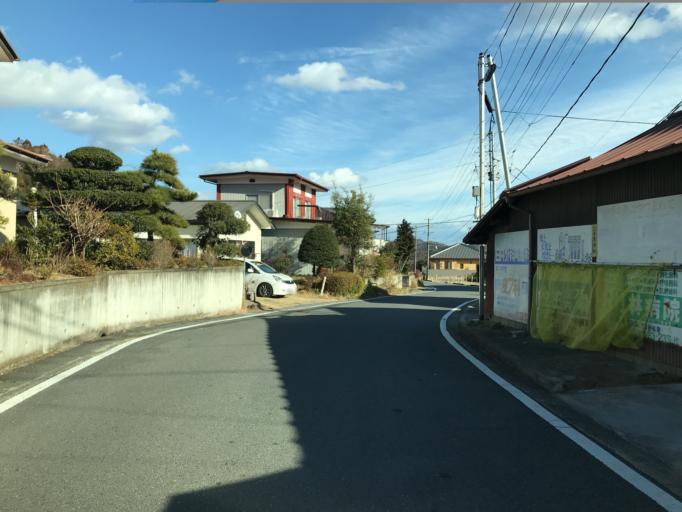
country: JP
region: Fukushima
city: Iwaki
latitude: 37.1268
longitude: 140.8464
